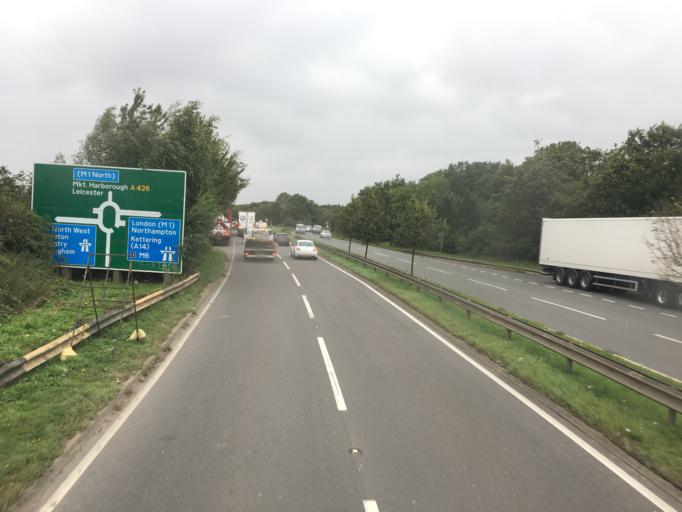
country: GB
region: England
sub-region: Warwickshire
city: Rugby
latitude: 52.4056
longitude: -1.2455
